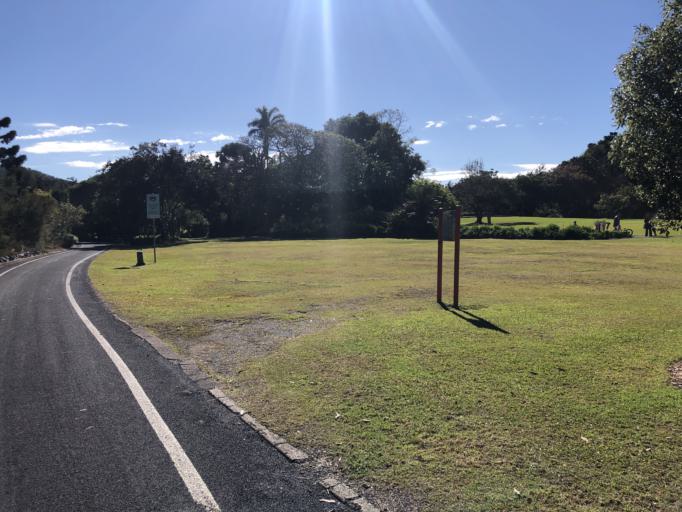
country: AU
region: New South Wales
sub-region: Coffs Harbour
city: Coffs Harbour
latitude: -30.2939
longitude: 153.1246
